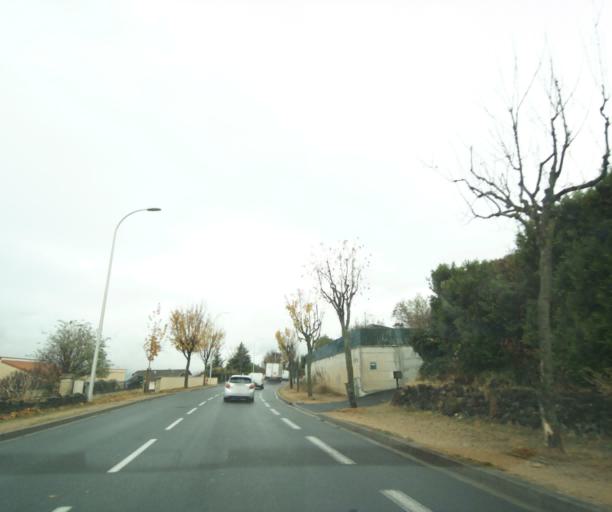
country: FR
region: Auvergne
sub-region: Departement du Puy-de-Dome
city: Cournon-d'Auvergne
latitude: 45.7410
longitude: 3.1852
